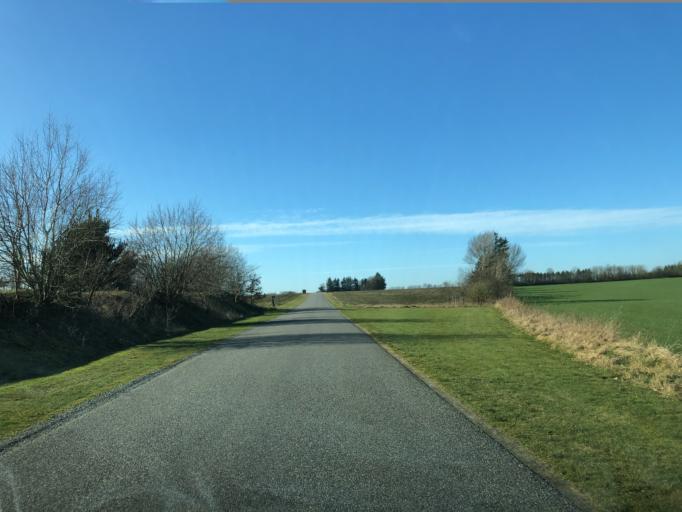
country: DK
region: Central Jutland
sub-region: Ikast-Brande Kommune
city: Bording Kirkeby
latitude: 56.1549
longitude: 9.2606
